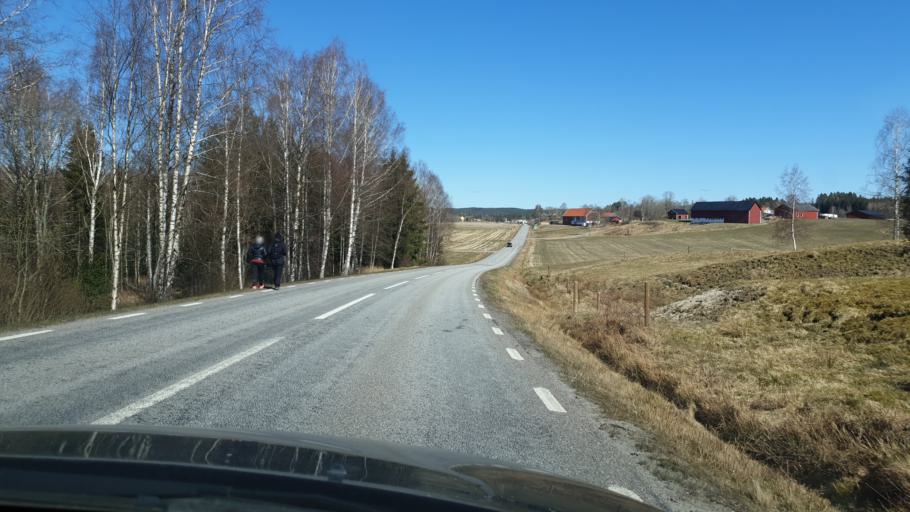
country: SE
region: Vaestra Goetaland
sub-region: Tanums Kommun
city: Tanumshede
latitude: 58.7618
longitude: 11.5501
